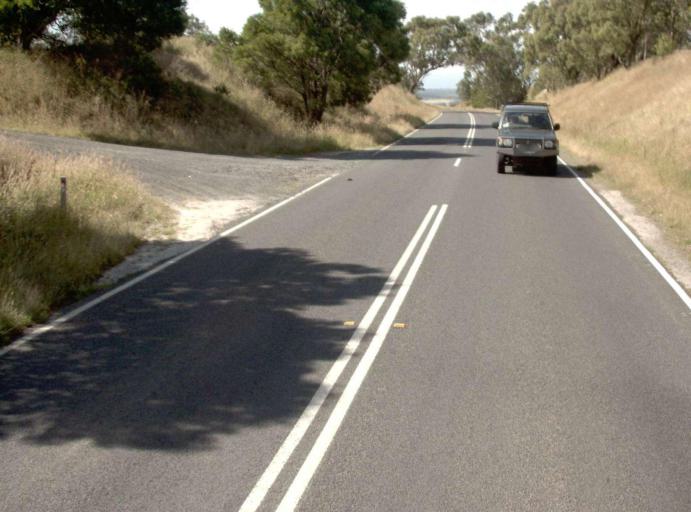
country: AU
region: Victoria
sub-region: Baw Baw
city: Warragul
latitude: -38.3239
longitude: 145.7692
